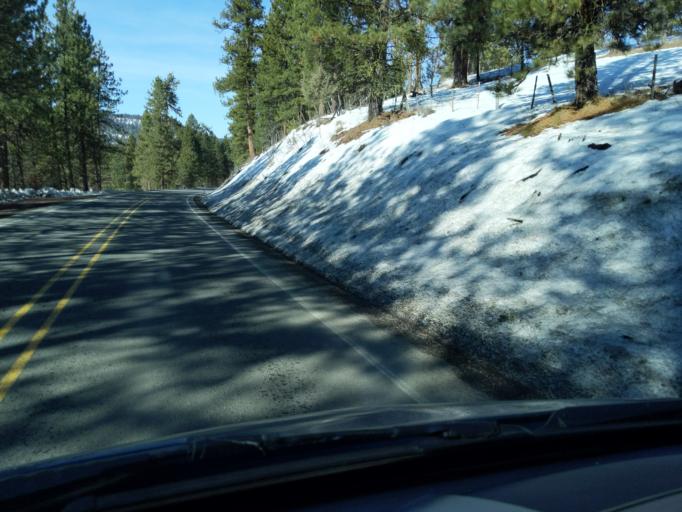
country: US
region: Oregon
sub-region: Grant County
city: John Day
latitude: 44.9168
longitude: -119.0092
